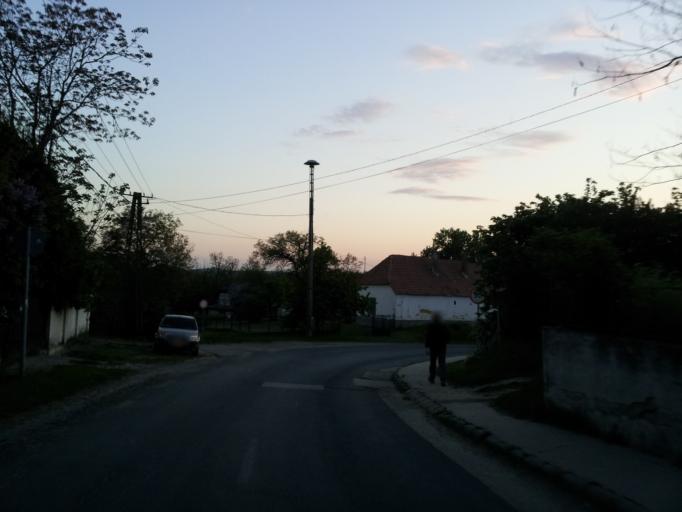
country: HU
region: Komarom-Esztergom
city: Csolnok
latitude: 47.6425
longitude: 18.7378
